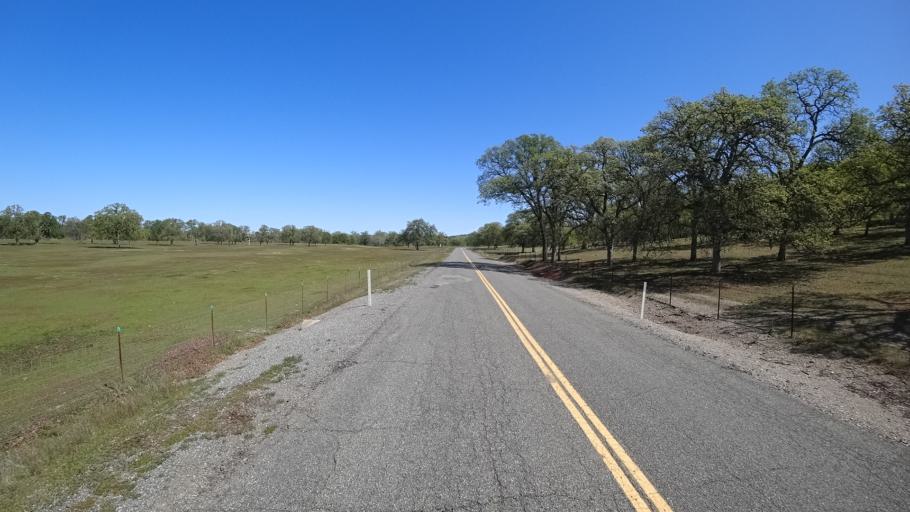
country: US
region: California
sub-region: Glenn County
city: Orland
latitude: 39.7333
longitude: -122.4013
